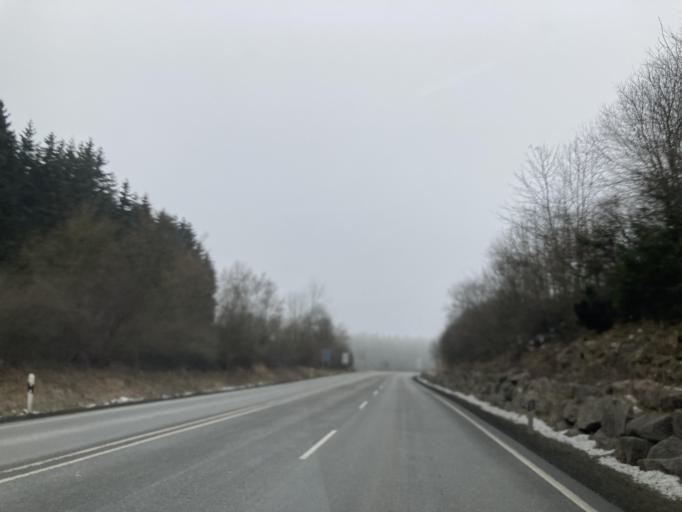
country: DE
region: Baden-Wuerttemberg
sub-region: Freiburg Region
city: Emmingen-Liptingen
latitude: 47.9494
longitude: 8.8862
